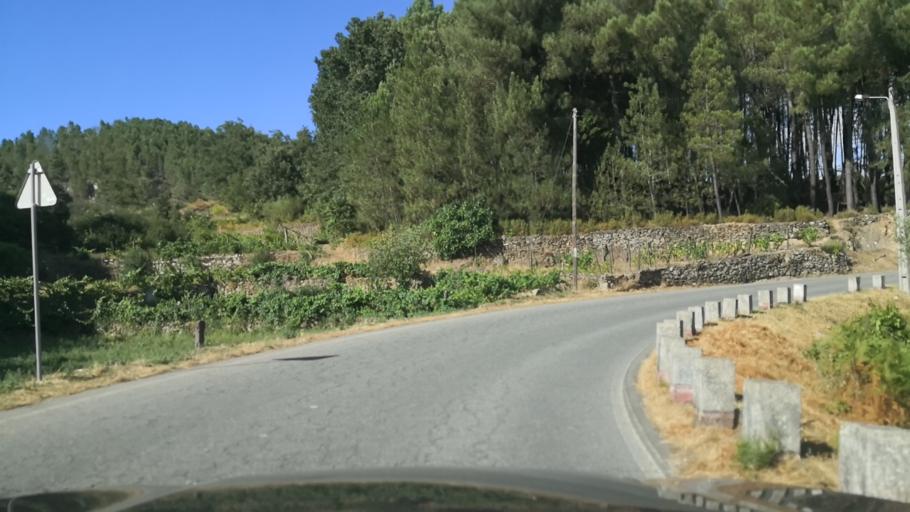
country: PT
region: Vila Real
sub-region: Sabrosa
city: Sabrosa
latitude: 41.3538
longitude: -7.5871
